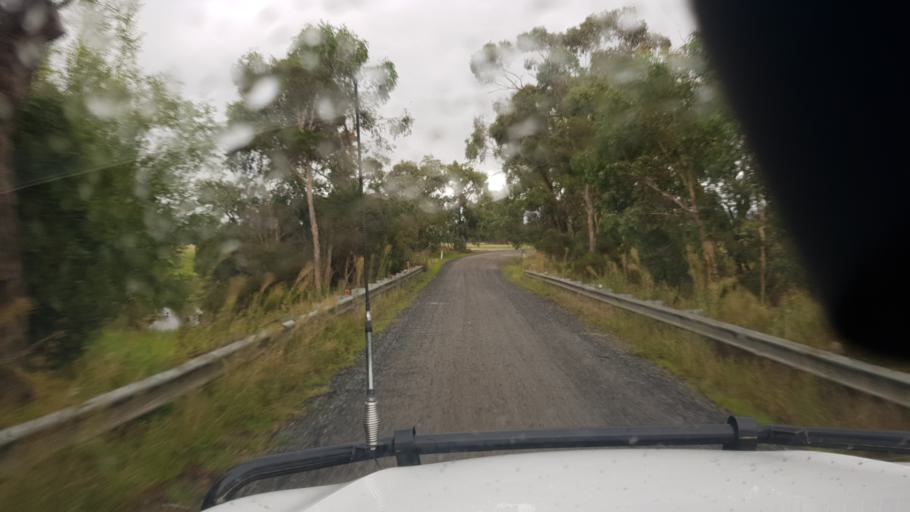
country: AU
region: Victoria
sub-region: Cardinia
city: Bunyip
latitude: -38.0520
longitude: 145.7659
